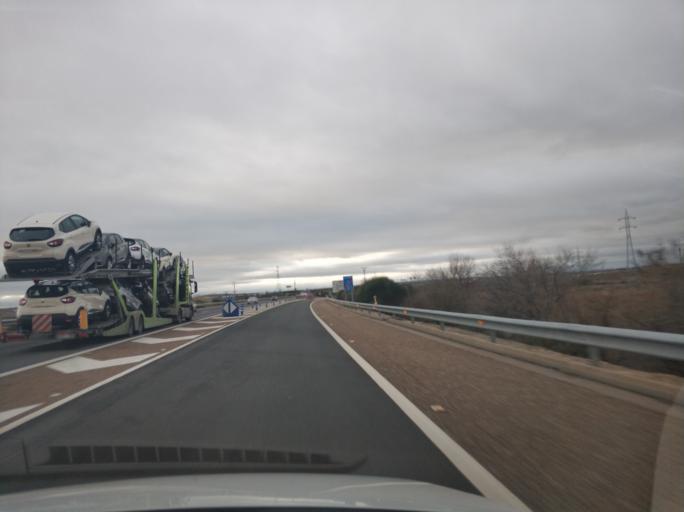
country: ES
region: Castille and Leon
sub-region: Provincia de Salamanca
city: Cabrerizos
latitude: 41.0014
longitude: -5.6179
